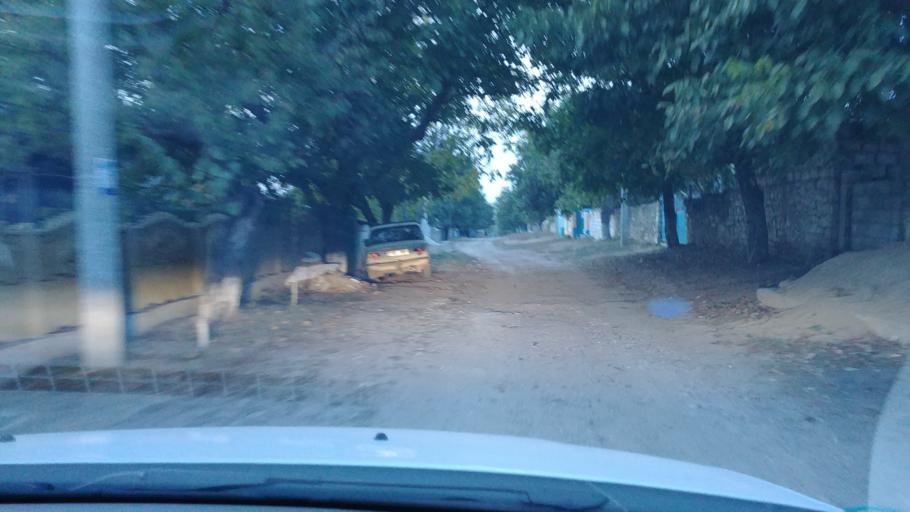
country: MD
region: Rezina
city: Saharna
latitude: 47.6770
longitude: 28.9602
